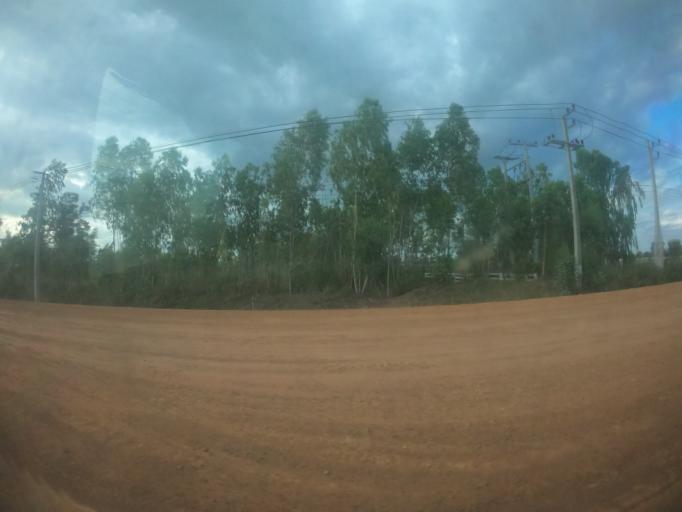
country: TH
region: Surin
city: Kap Choeng
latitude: 14.4585
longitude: 103.6683
